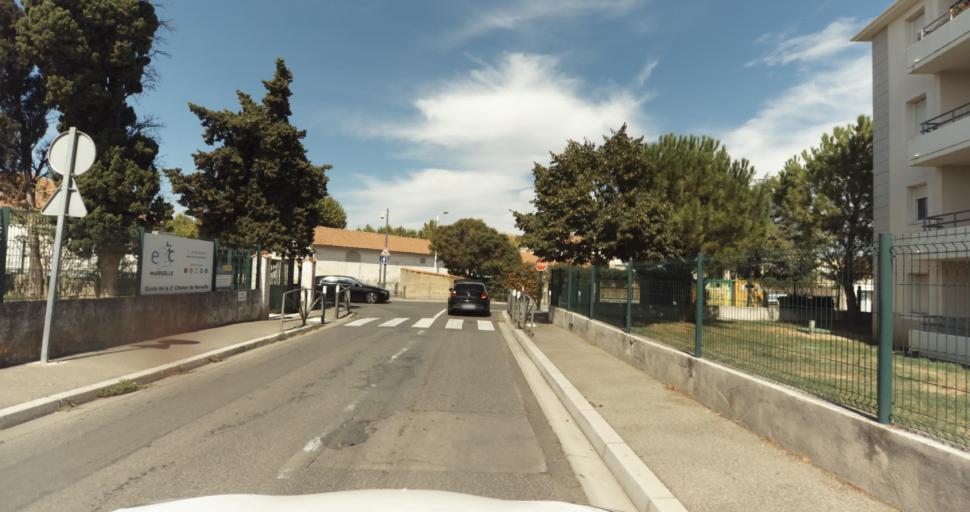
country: FR
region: Provence-Alpes-Cote d'Azur
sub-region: Departement des Bouches-du-Rhone
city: Miramas
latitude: 43.5826
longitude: 5.0056
